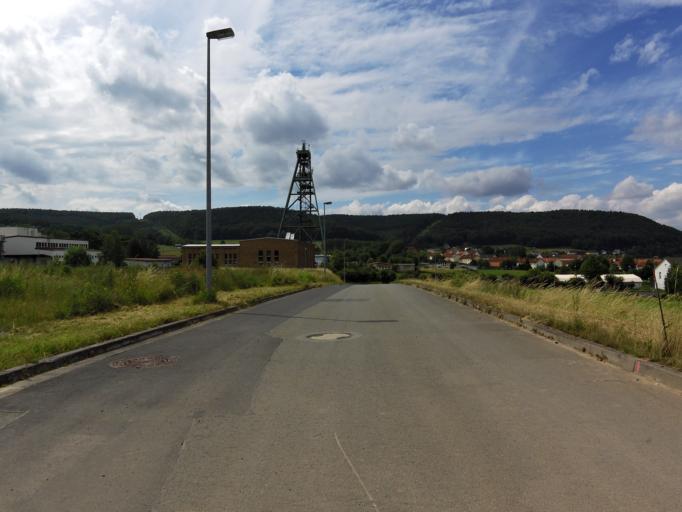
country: DE
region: Thuringia
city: Stadtlengsfeld
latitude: 50.8193
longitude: 10.1250
